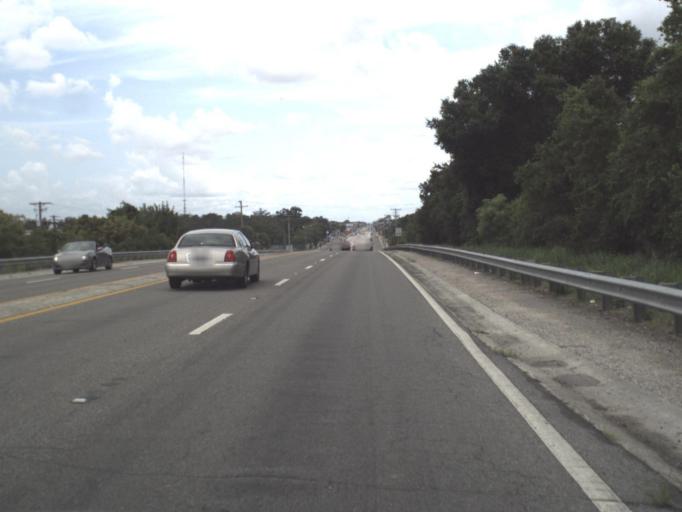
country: US
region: Florida
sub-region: Hillsborough County
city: East Lake-Orient Park
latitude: 27.9962
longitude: -82.3982
